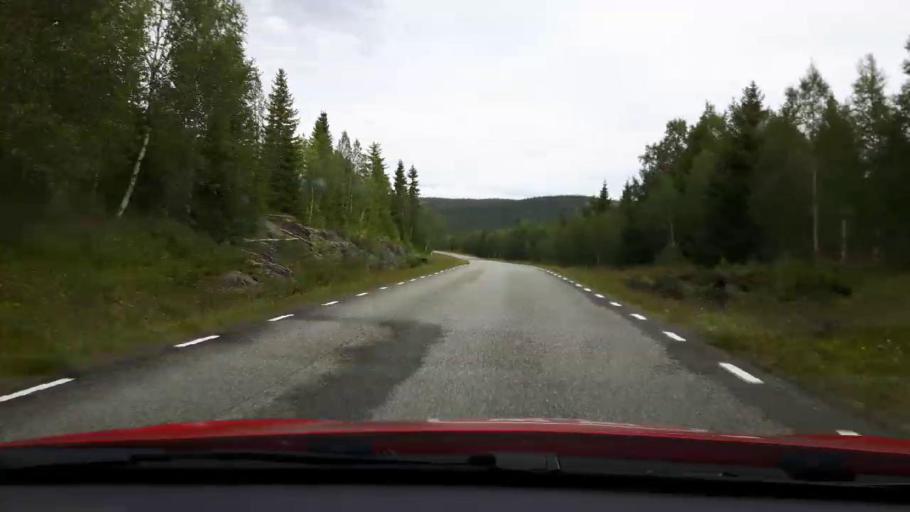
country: SE
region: Jaemtland
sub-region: Are Kommun
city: Are
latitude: 63.7352
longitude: 13.0681
